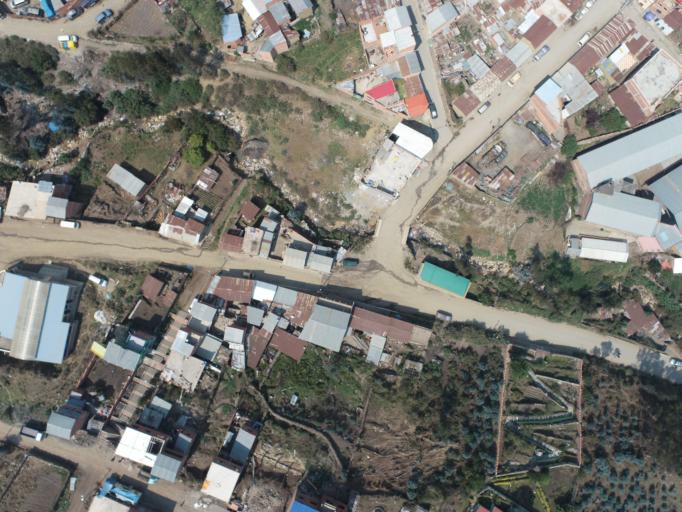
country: BO
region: La Paz
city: Quime
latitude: -16.9824
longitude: -67.2148
